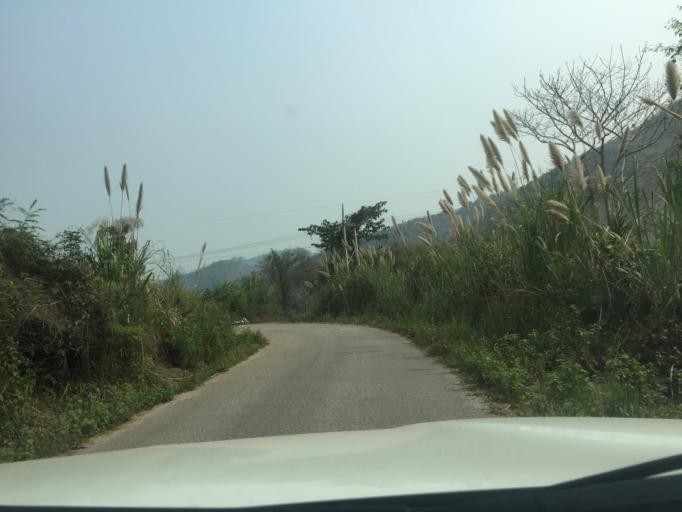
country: LA
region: Xiagnabouli
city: Sainyabuli
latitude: 19.3004
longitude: 101.4824
